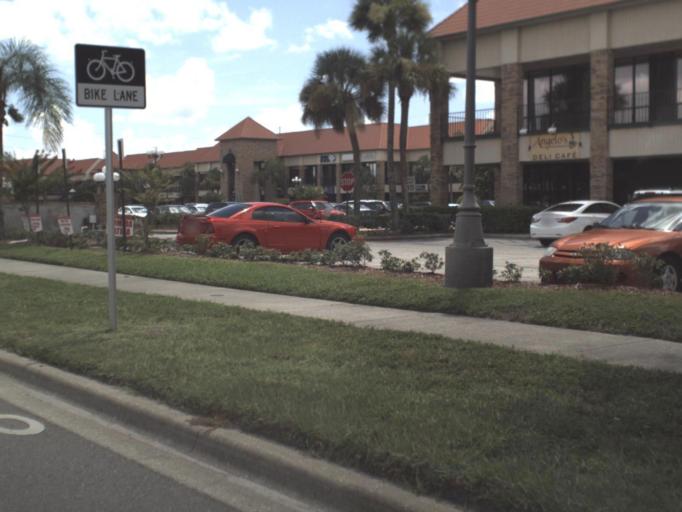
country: US
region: Florida
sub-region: Hillsborough County
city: Egypt Lake-Leto
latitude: 28.0098
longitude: -82.5052
